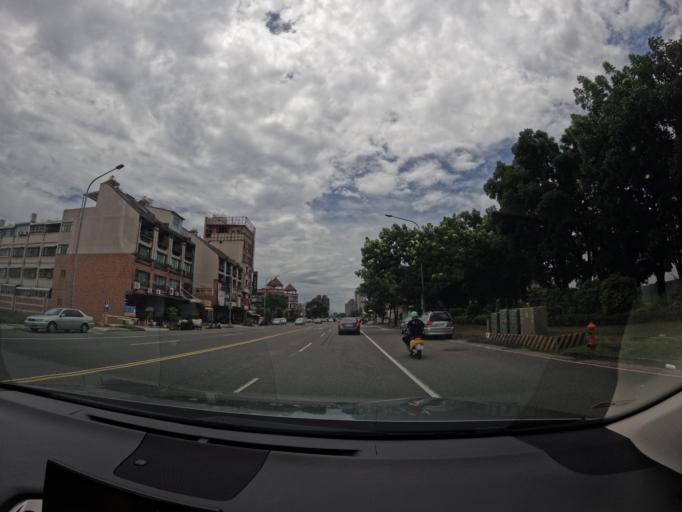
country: TW
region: Kaohsiung
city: Kaohsiung
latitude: 22.7271
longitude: 120.2927
